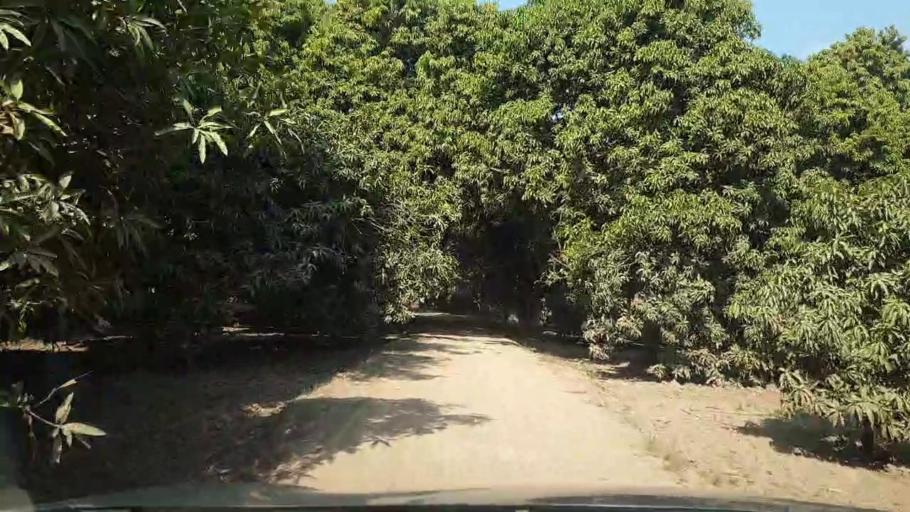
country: PK
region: Sindh
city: Tando Jam
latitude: 25.4686
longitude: 68.6225
